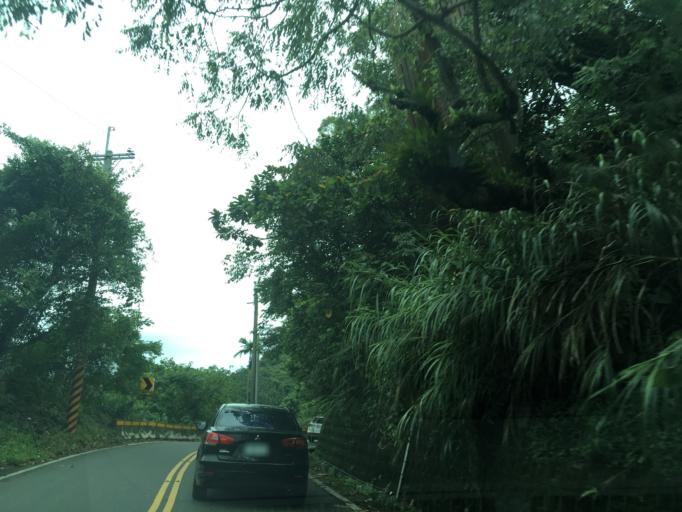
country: TW
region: Taiwan
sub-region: Yunlin
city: Douliu
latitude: 23.5641
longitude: 120.5912
